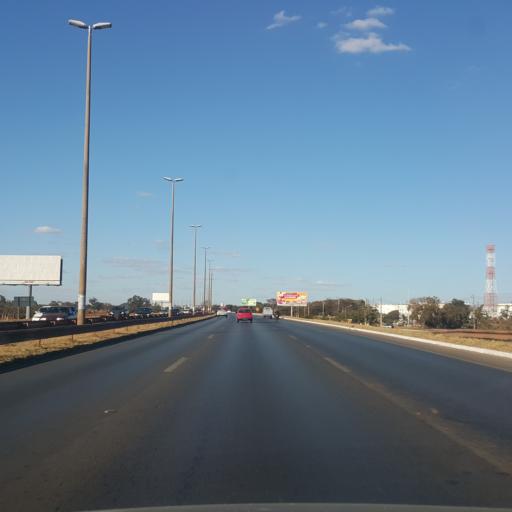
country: BR
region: Federal District
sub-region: Brasilia
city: Brasilia
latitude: -15.7951
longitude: -47.9626
